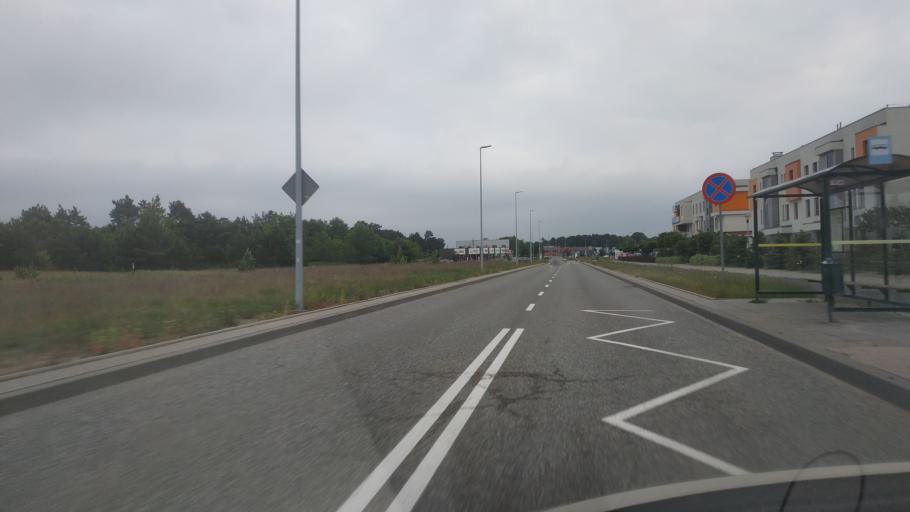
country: PL
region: Kujawsko-Pomorskie
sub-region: Torun
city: Torun
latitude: 53.0437
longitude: 18.6009
